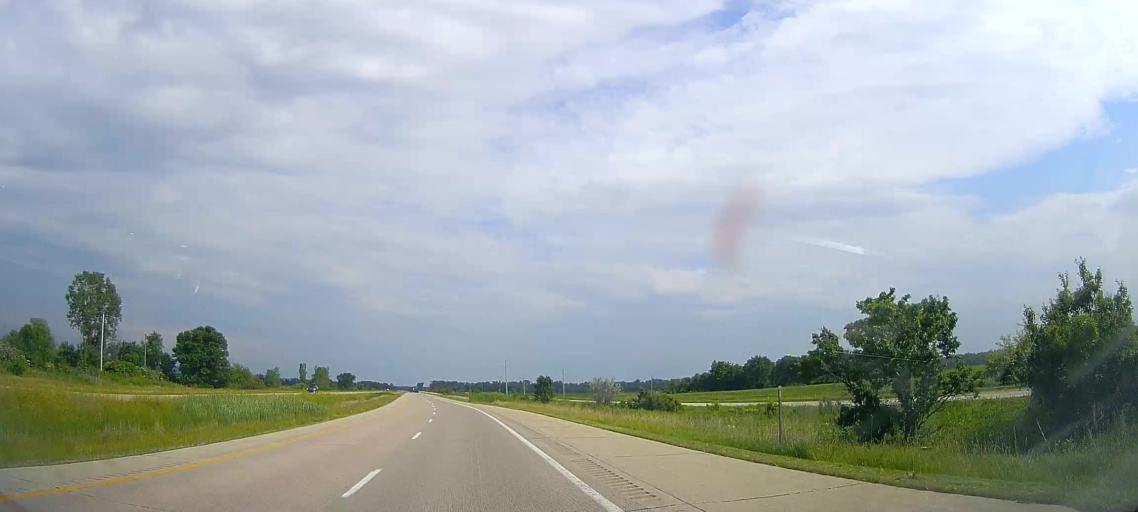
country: US
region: Nebraska
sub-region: Burt County
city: Tekamah
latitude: 41.8512
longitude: -96.1002
